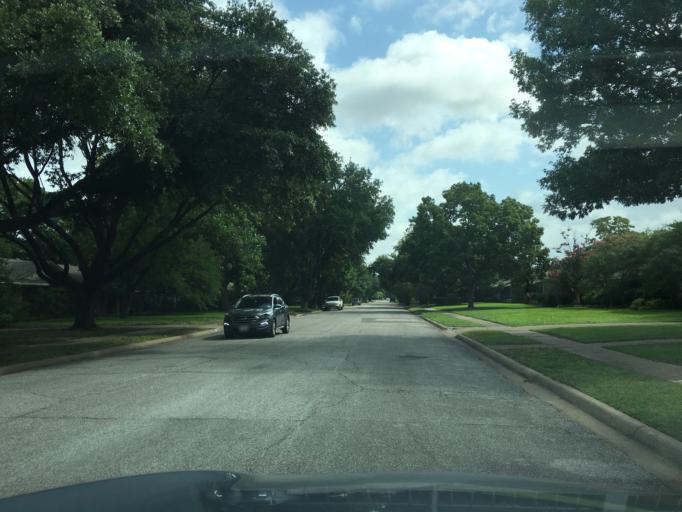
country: US
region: Texas
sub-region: Dallas County
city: Richardson
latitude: 32.9403
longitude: -96.7249
